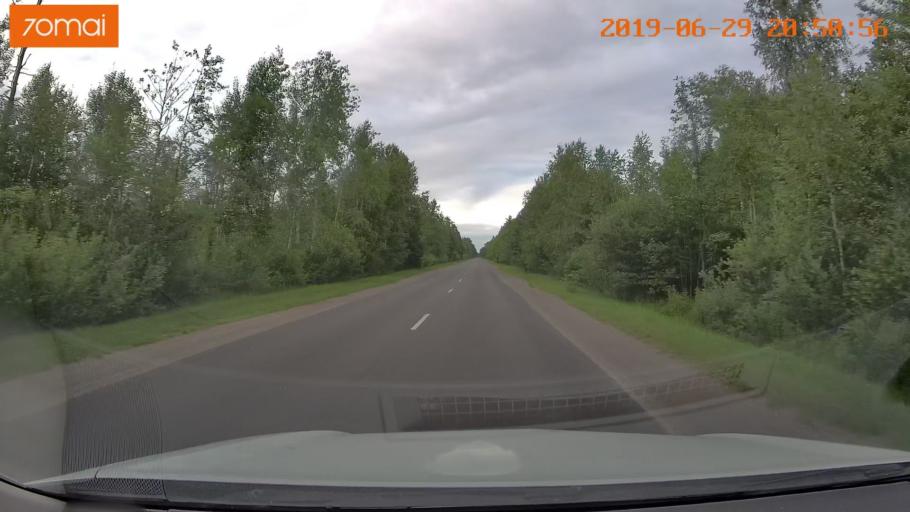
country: BY
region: Brest
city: Hantsavichy
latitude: 52.6822
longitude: 26.3425
